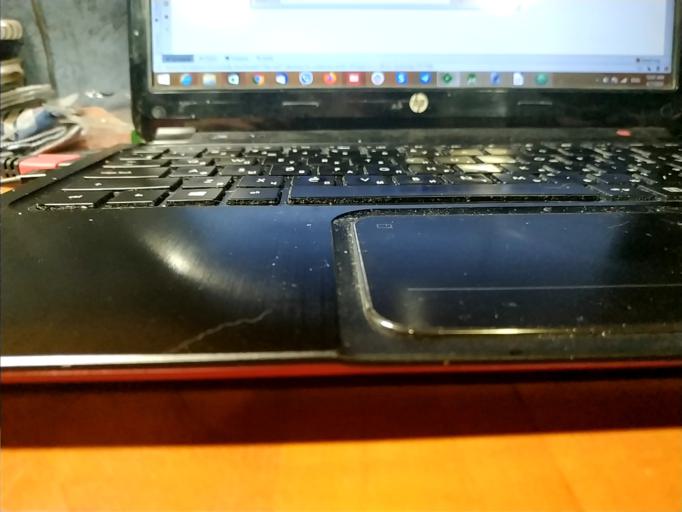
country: RU
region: Vologda
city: Suda
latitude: 58.9150
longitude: 37.5432
